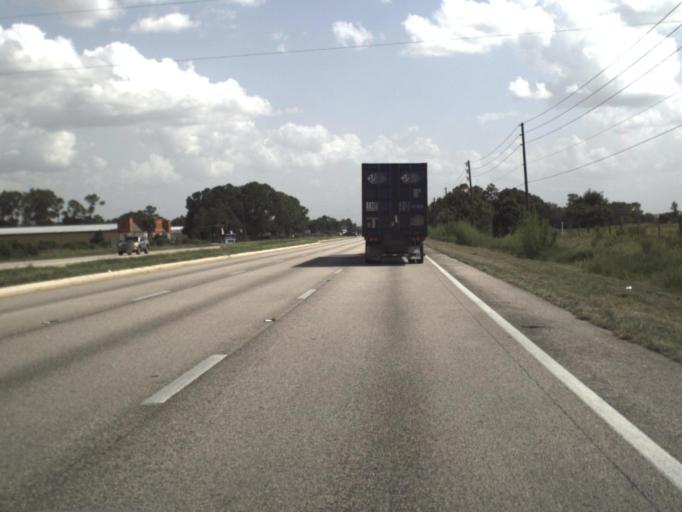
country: US
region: Florida
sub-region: Polk County
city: Lake Wales
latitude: 27.9433
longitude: -81.6148
